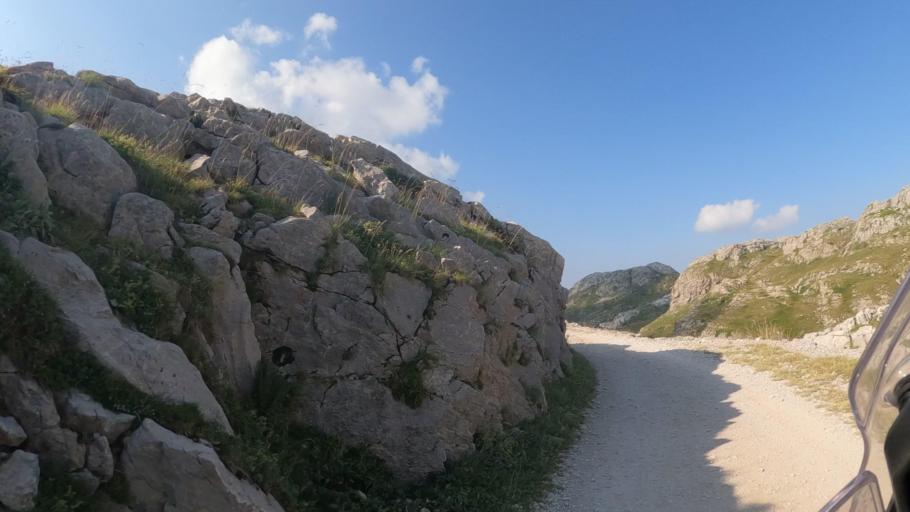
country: IT
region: Piedmont
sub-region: Provincia di Cuneo
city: Limone Piemonte
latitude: 44.1666
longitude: 7.6683
